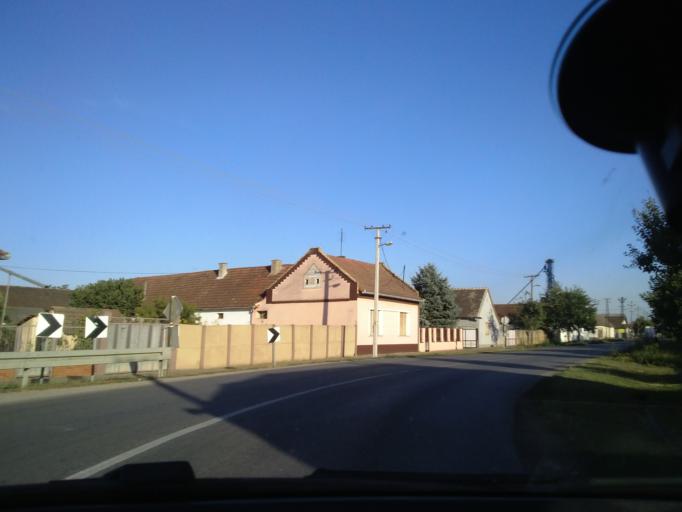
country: RS
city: Maglic
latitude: 45.3972
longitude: 19.4549
